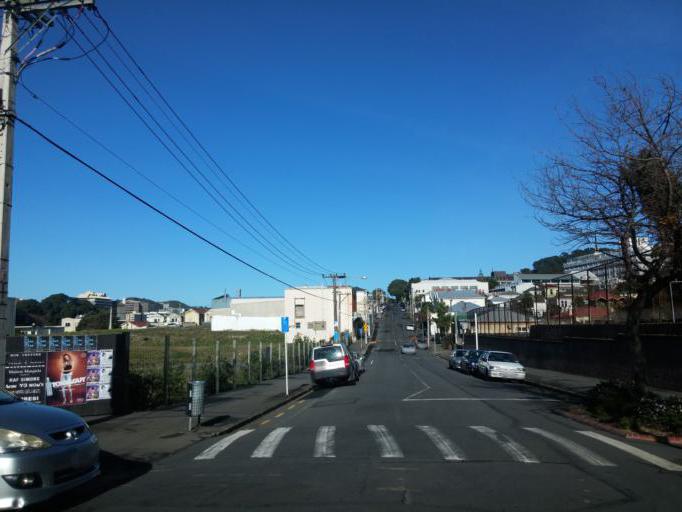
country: NZ
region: Wellington
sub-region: Wellington City
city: Wellington
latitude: -41.3004
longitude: 174.7778
